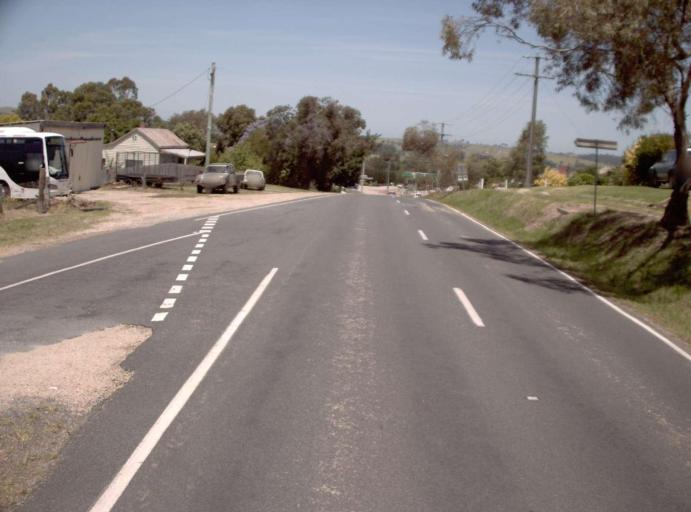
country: AU
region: Victoria
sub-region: East Gippsland
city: Lakes Entrance
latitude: -37.7058
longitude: 147.8340
